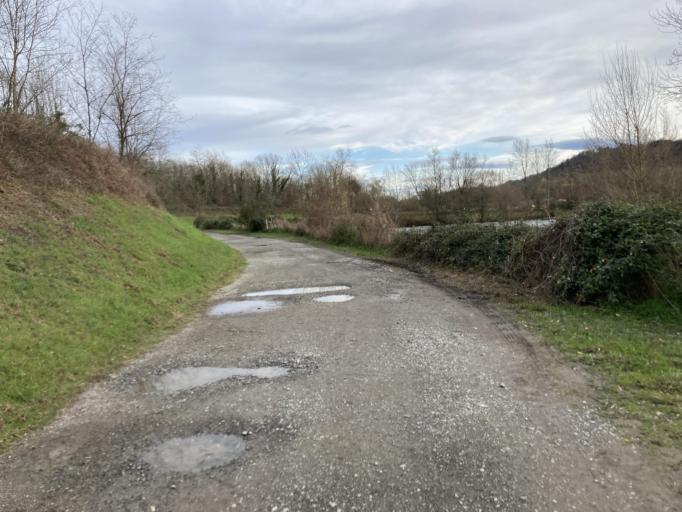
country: FR
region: Aquitaine
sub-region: Departement des Pyrenees-Atlantiques
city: Artiguelouve
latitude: 43.3105
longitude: -0.4398
